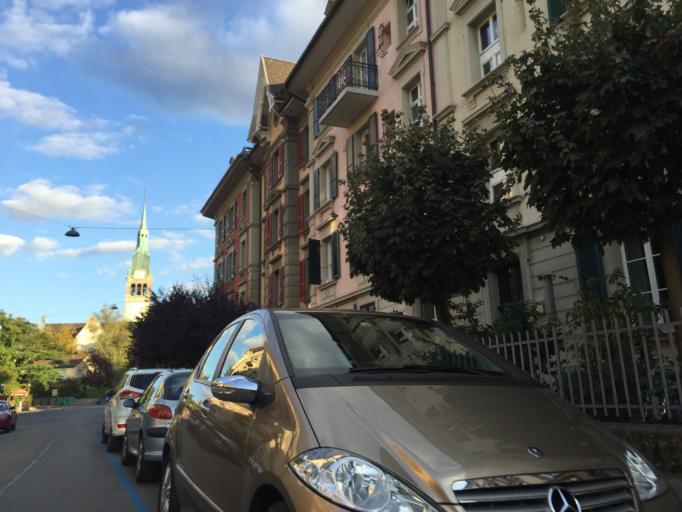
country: CH
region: Bern
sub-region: Bern-Mittelland District
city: Bern
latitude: 46.9537
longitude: 7.4277
